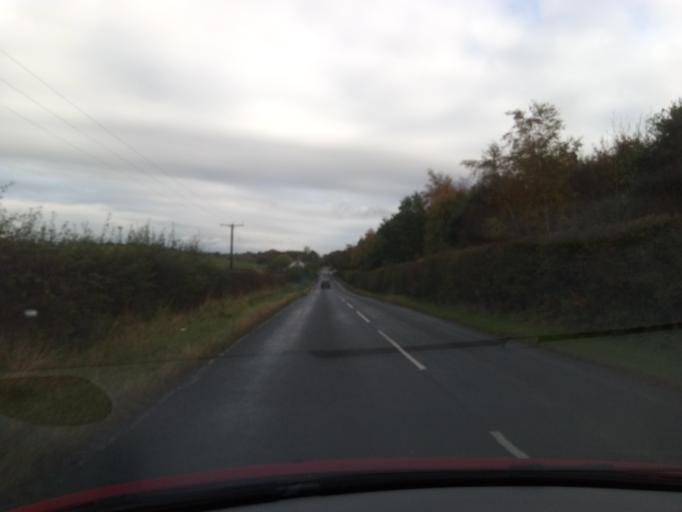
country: GB
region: Scotland
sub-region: The Scottish Borders
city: Saint Boswells
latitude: 55.5670
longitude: -2.6639
